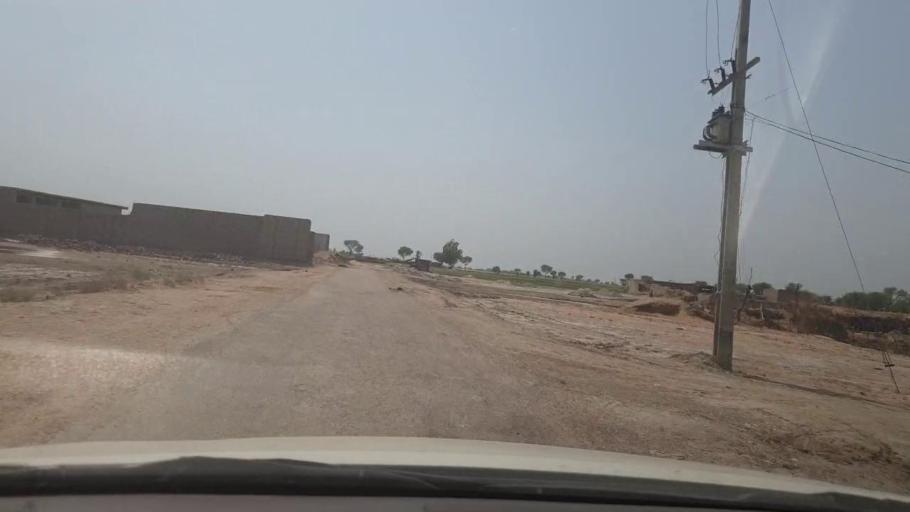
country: PK
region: Sindh
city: Shikarpur
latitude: 27.9934
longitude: 68.5739
